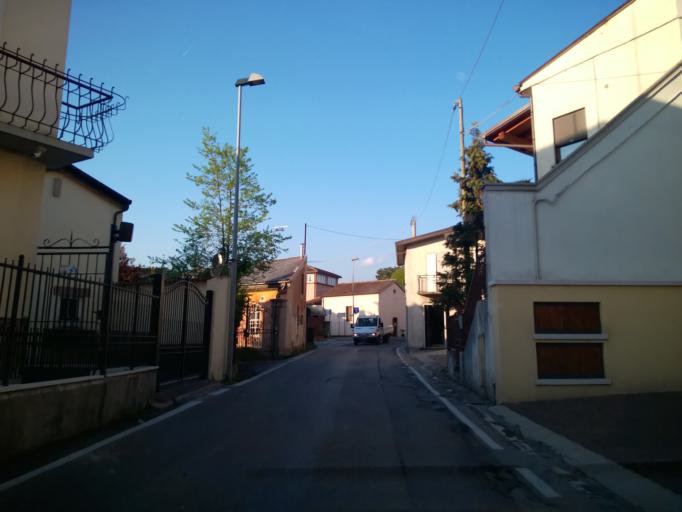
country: IT
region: Veneto
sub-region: Provincia di Vicenza
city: Marano Vicentino
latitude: 45.6943
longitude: 11.4315
